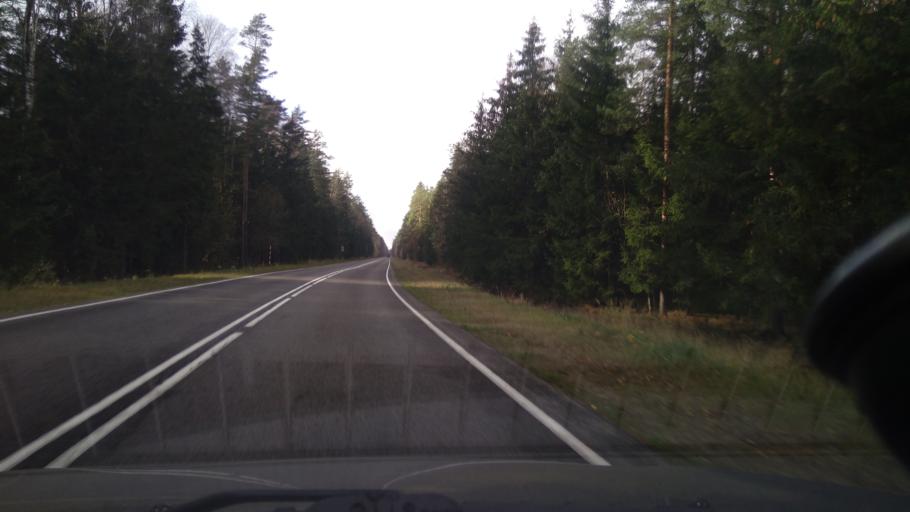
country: BY
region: Minsk
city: Urechcha
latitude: 53.2058
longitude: 27.7997
